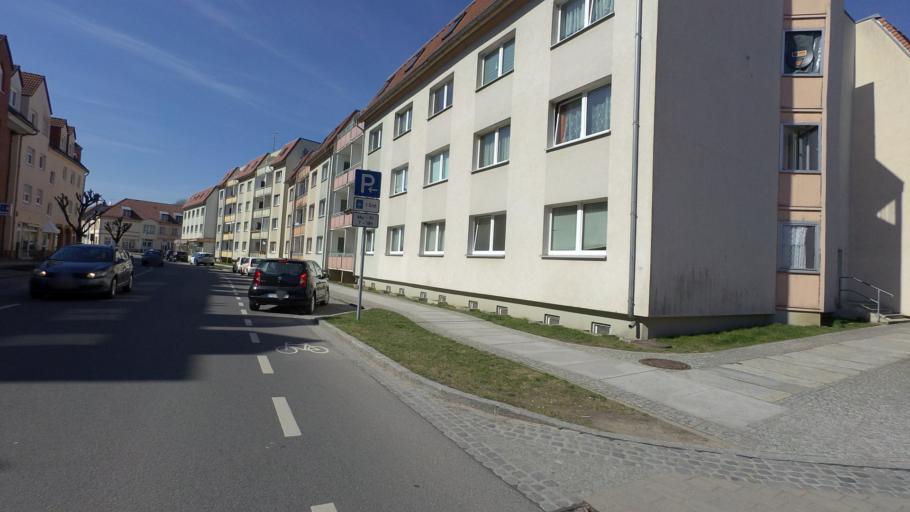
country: DE
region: Brandenburg
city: Muncheberg
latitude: 52.5024
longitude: 14.1419
